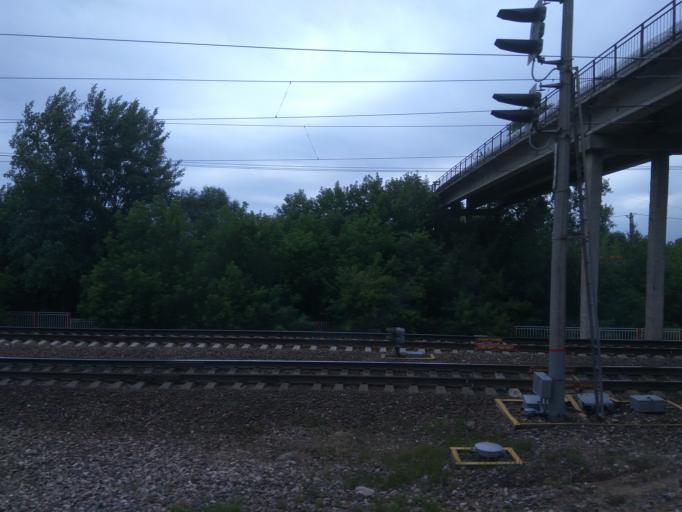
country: RU
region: Tatarstan
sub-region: Gorod Kazan'
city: Kazan
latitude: 55.8424
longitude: 49.0714
